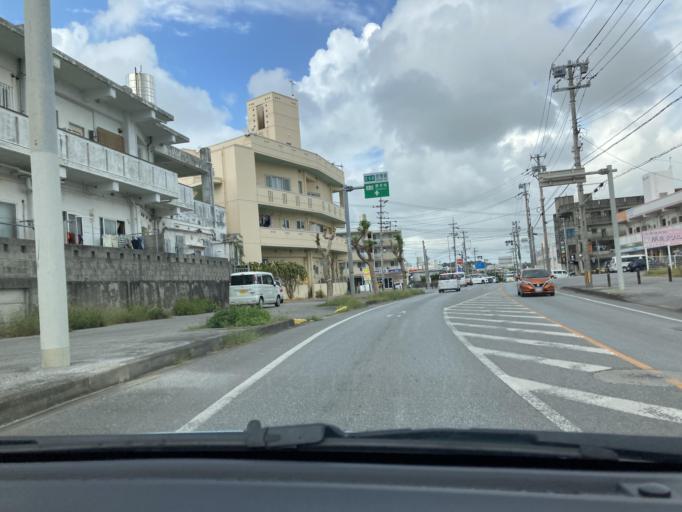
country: JP
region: Okinawa
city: Itoman
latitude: 26.1336
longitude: 127.6866
